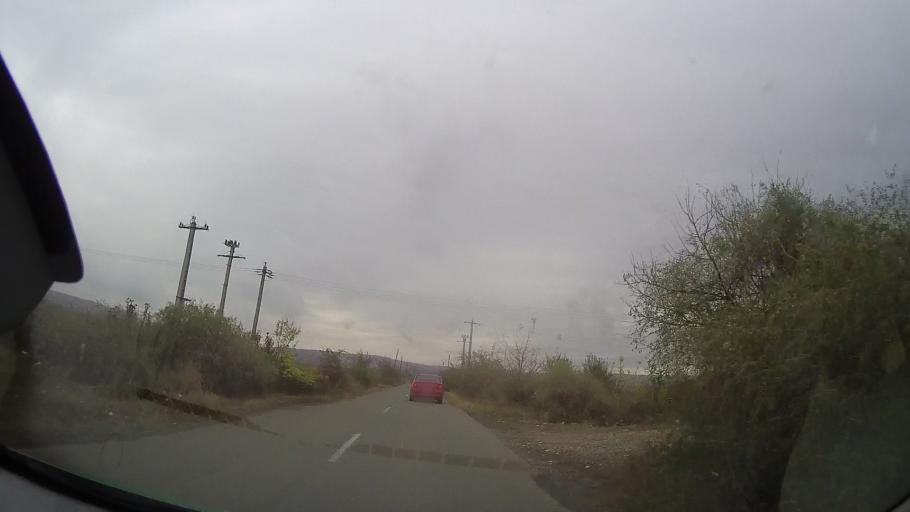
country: RO
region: Prahova
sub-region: Comuna Fantanele
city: Fantanele
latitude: 45.0164
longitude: 26.3803
